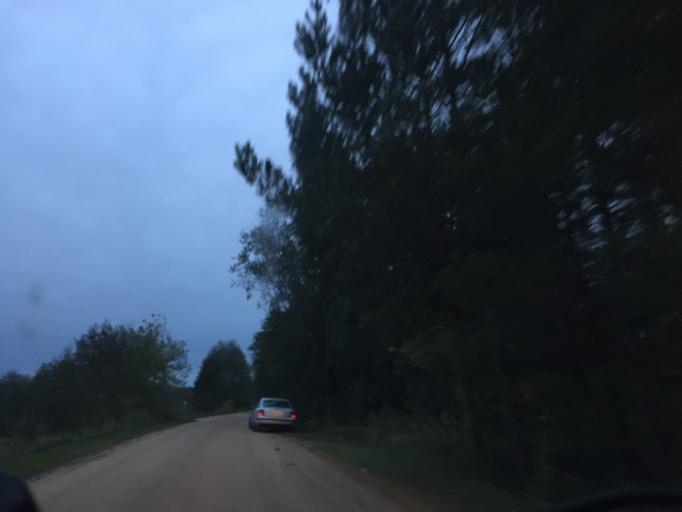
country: LV
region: Adazi
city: Adazi
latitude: 57.0801
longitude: 24.3700
